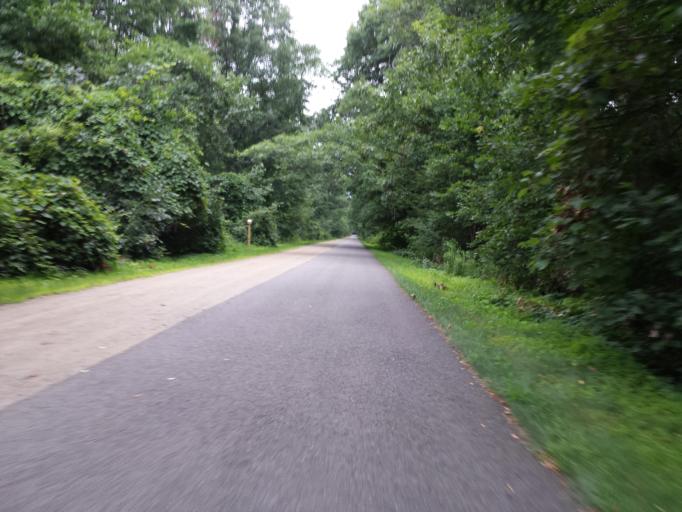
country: US
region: New York
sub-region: Dutchess County
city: Hillside Lake
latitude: 41.5879
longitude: -73.8211
